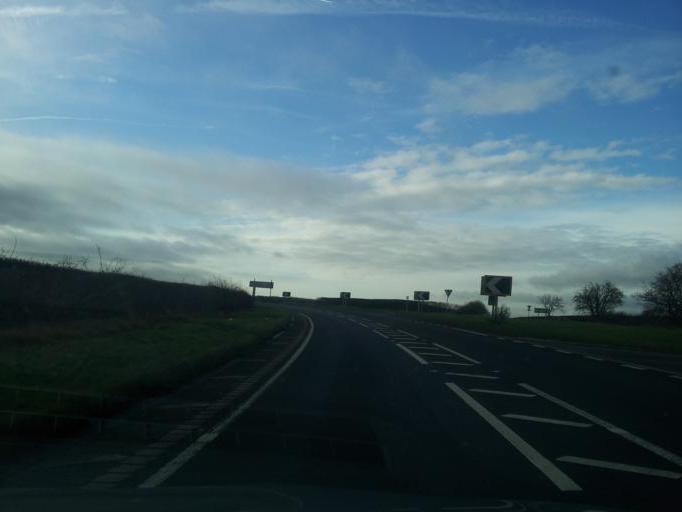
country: GB
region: England
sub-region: District of Rutland
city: Ketton
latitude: 52.5869
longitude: -0.5568
